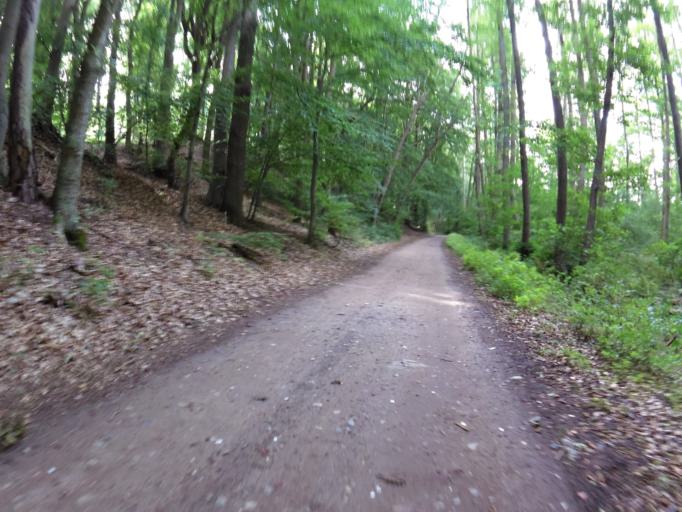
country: DE
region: Mecklenburg-Vorpommern
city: Seebad Bansin
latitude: 53.9720
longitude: 14.1074
